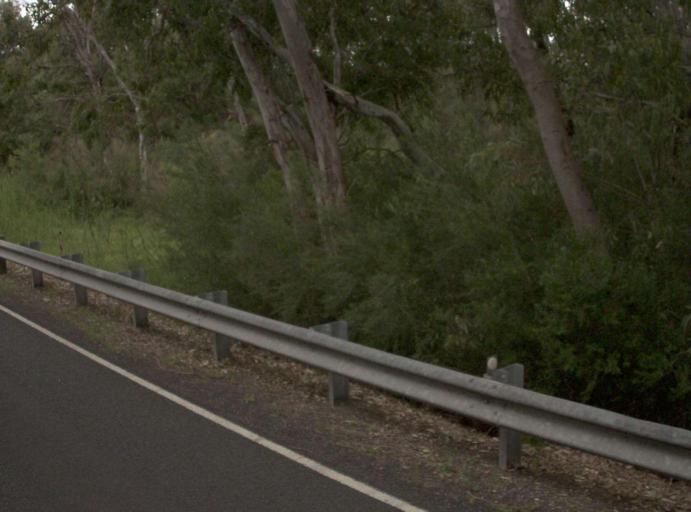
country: AU
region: Victoria
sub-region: Wellington
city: Sale
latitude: -38.0217
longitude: 147.1813
